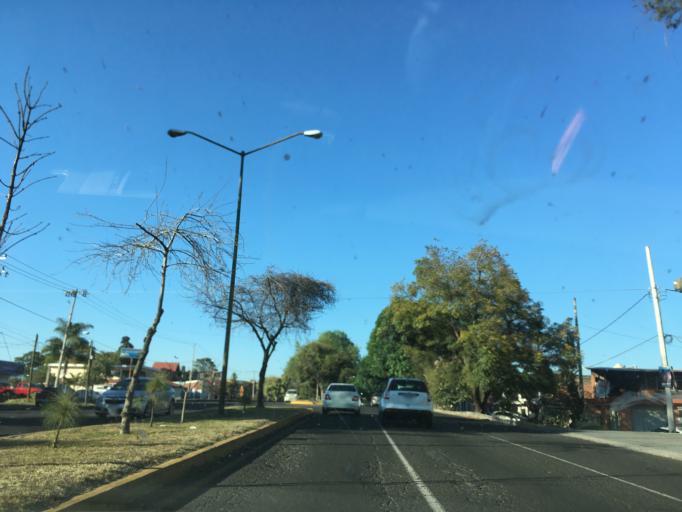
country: MX
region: Michoacan
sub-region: Uruapan
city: Santa Rosa (Santa Barbara)
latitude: 19.3851
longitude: -102.0595
